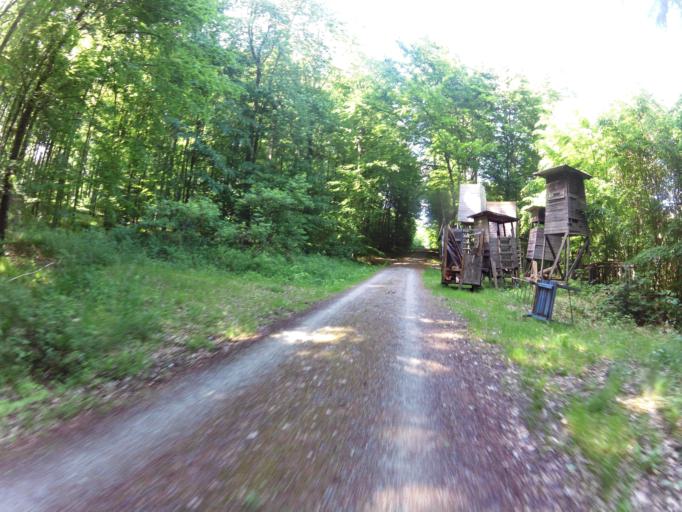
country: DE
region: Bavaria
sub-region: Regierungsbezirk Unterfranken
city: Uettingen
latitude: 49.7847
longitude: 9.7426
